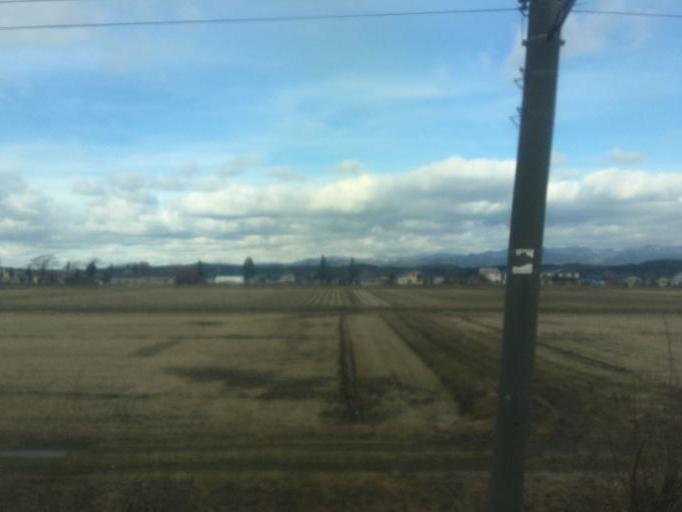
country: JP
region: Akita
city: Noshiromachi
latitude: 40.2150
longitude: 140.1619
